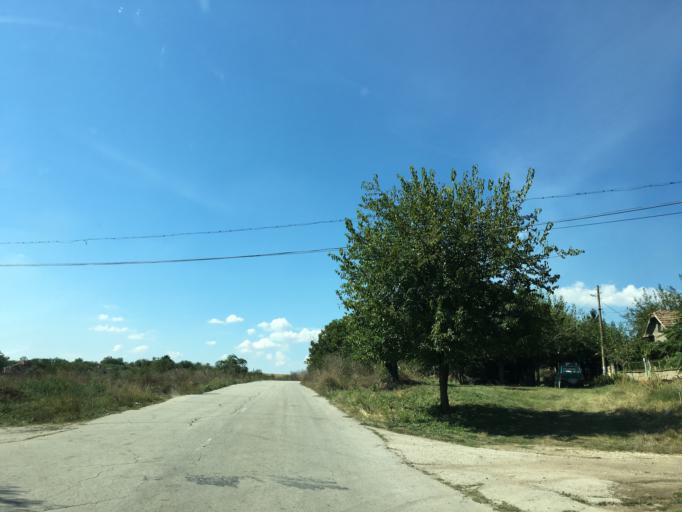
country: RO
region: Olt
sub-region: Comuna Orlea
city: Orlea
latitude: 43.6383
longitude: 24.3921
